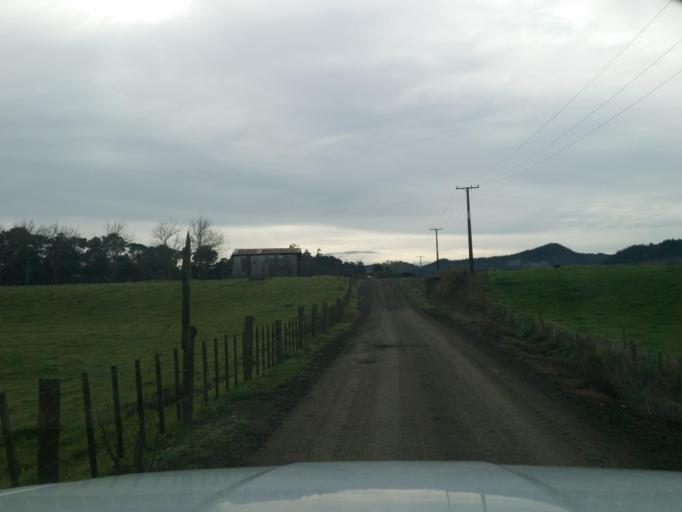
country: NZ
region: Northland
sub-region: Whangarei
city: Maungatapere
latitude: -35.7988
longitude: 174.0538
